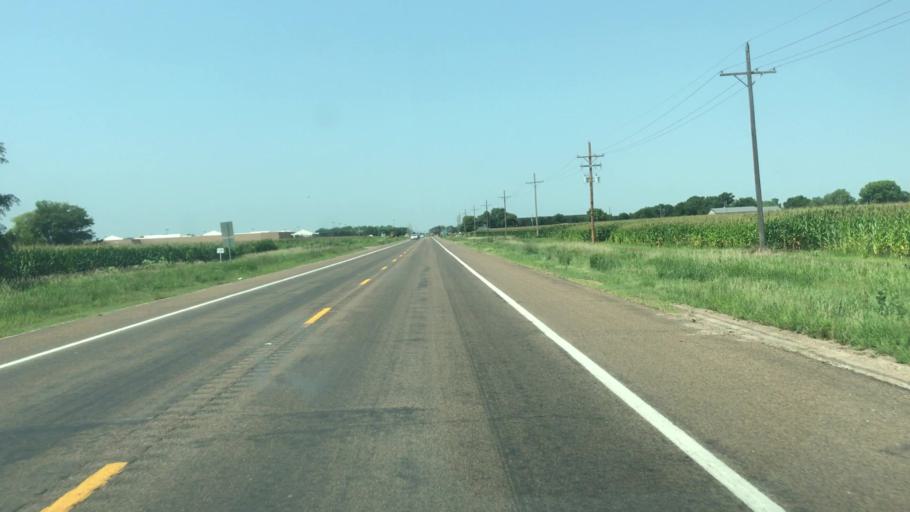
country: US
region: Nebraska
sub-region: Hall County
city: Grand Island
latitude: 40.8870
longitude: -98.3287
